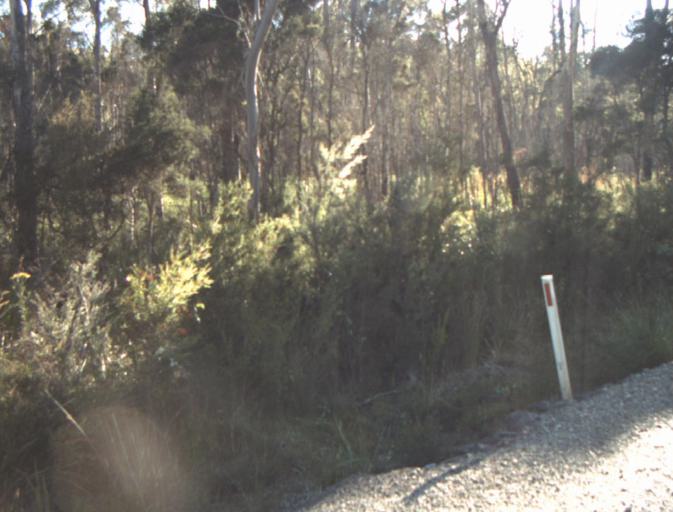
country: AU
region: Tasmania
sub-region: Launceston
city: Mayfield
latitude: -41.3355
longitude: 147.1934
